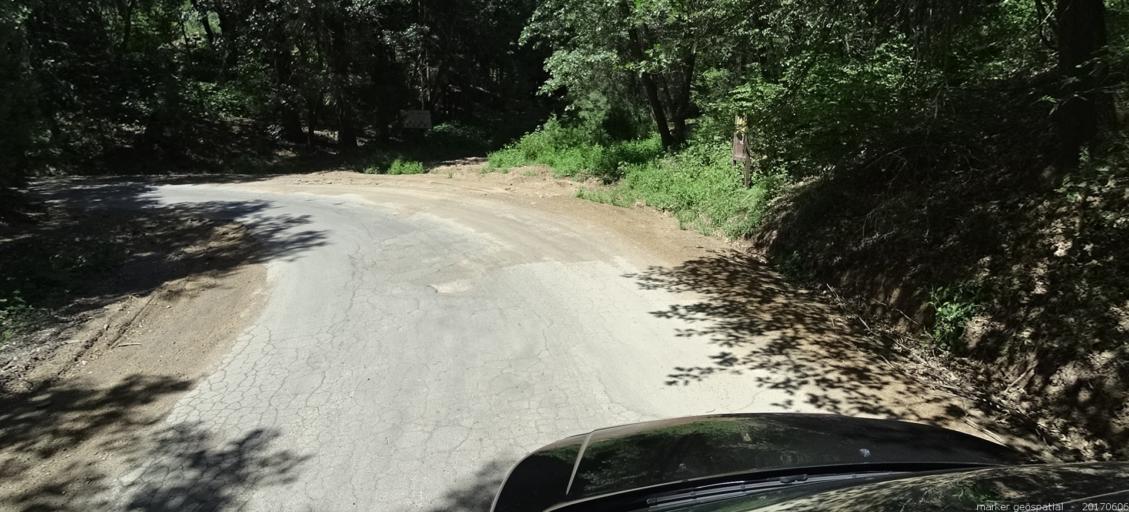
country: US
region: California
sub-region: Siskiyou County
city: Mount Shasta
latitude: 41.2747
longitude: -122.2974
